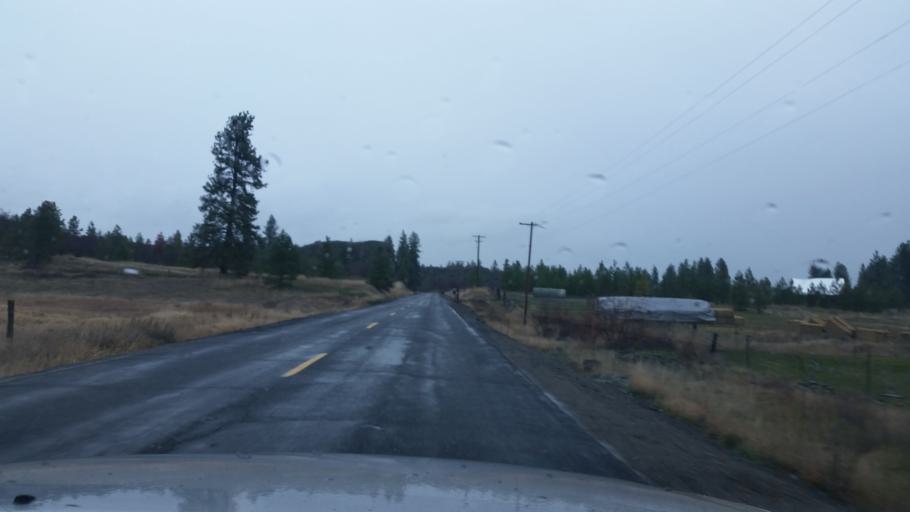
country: US
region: Washington
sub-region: Spokane County
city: Airway Heights
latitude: 47.6933
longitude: -117.5718
